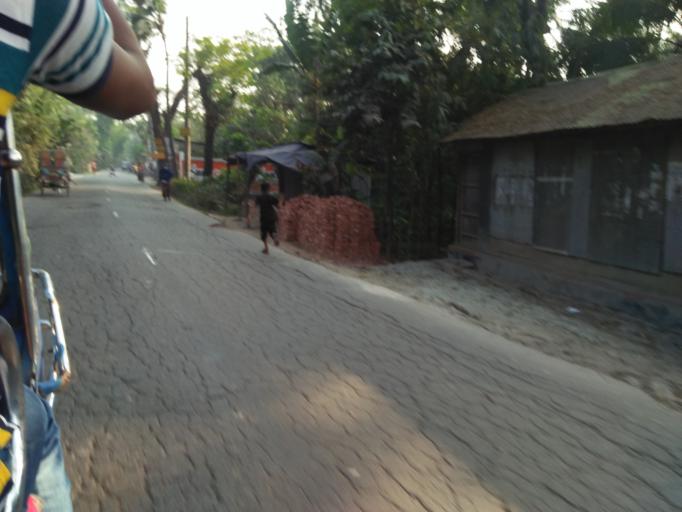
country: BD
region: Barisal
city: Bhola
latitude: 22.6984
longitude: 90.6429
